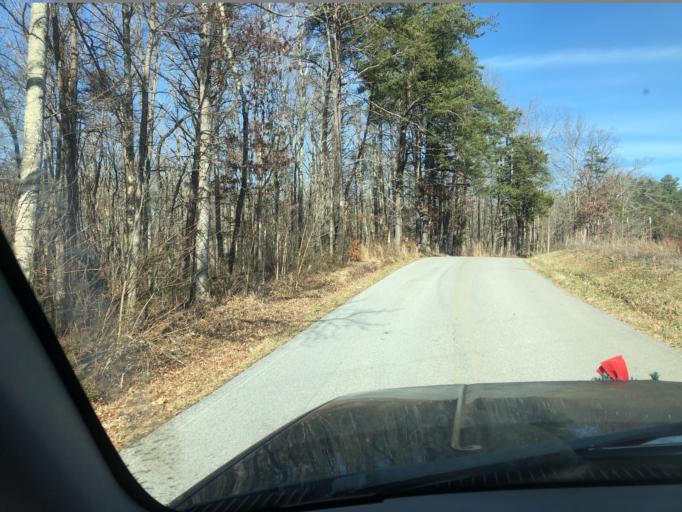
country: US
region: Tennessee
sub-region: Putnam County
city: Monterey
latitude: 36.0169
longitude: -85.2710
